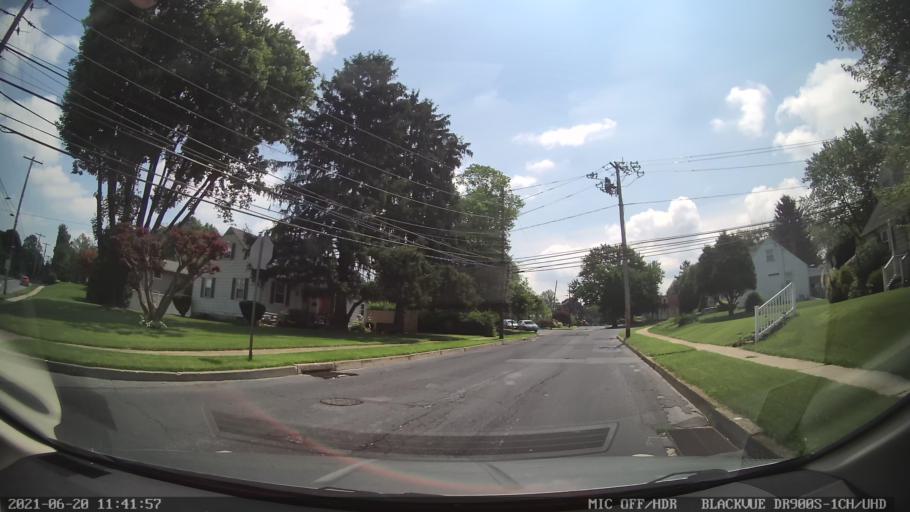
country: US
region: Pennsylvania
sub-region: Lehigh County
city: Dorneyville
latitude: 40.5859
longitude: -75.5138
